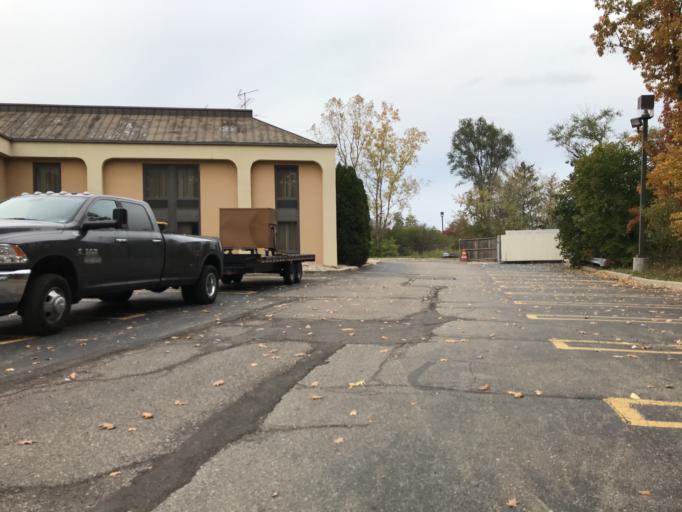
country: US
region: Michigan
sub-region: Oakland County
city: Bingham Farms
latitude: 42.4912
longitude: -83.2804
